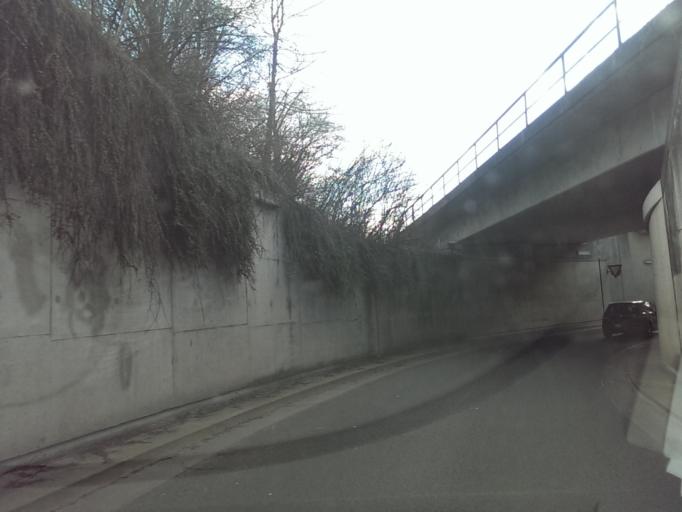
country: DE
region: Lower Saxony
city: Hildesheim
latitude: 52.1425
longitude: 9.9618
